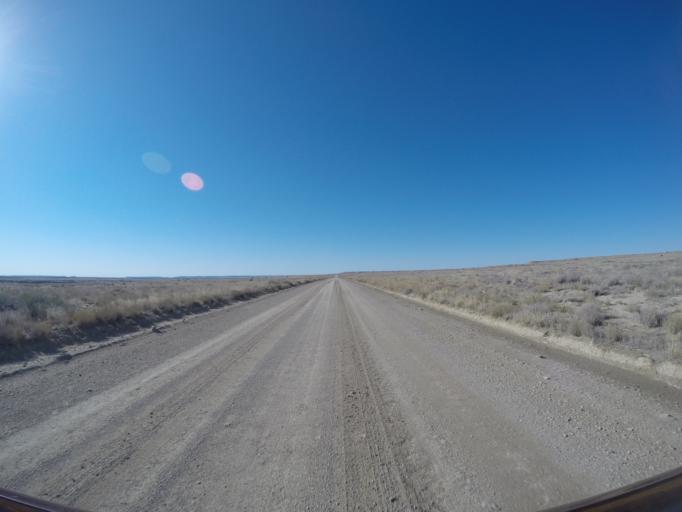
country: US
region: Colorado
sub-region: Otero County
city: La Junta
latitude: 37.7895
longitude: -103.5245
